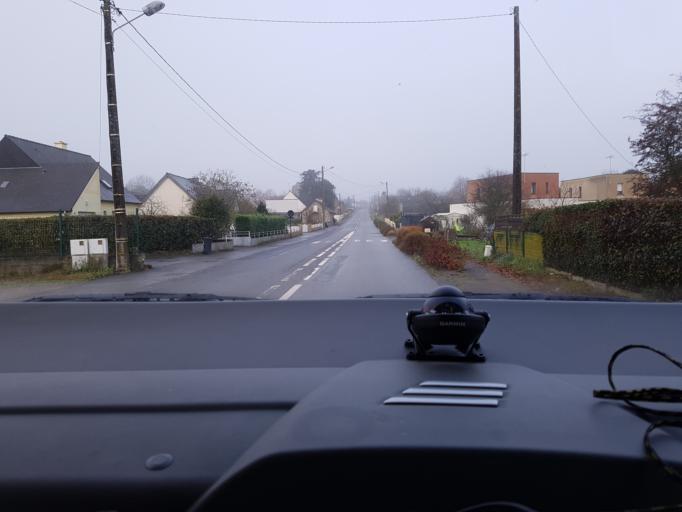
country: FR
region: Brittany
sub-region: Departement d'Ille-et-Vilaine
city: Livre-sur-Changeon
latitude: 48.1792
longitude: -1.3115
